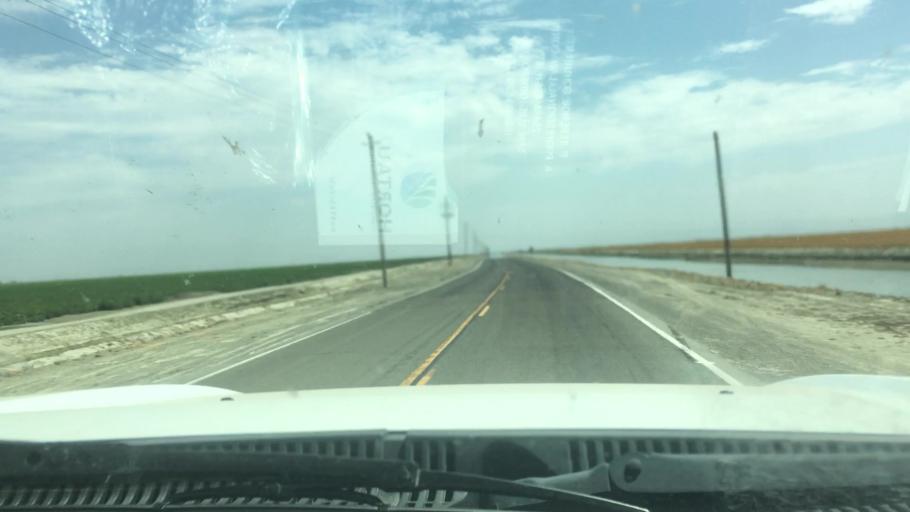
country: US
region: California
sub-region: Tulare County
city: Alpaugh
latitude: 35.8909
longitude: -119.5735
